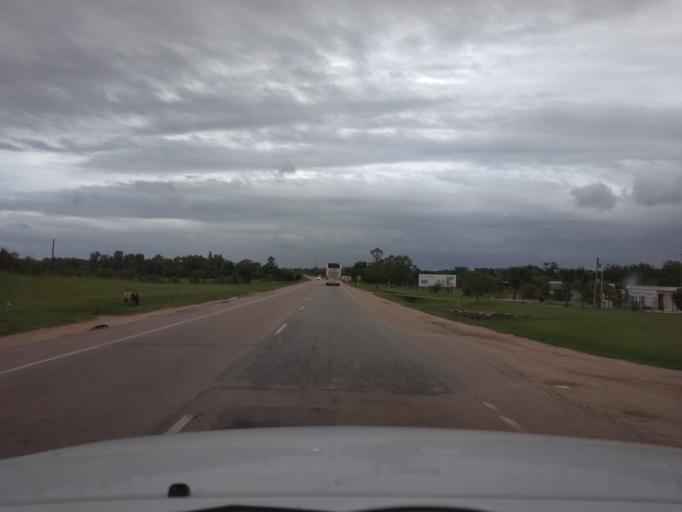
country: UY
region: Canelones
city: Canelones
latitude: -34.4952
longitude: -56.2820
